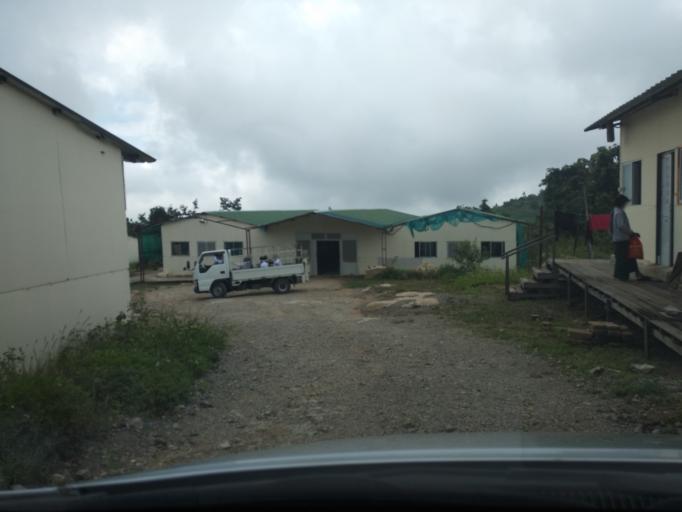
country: MM
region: Mandalay
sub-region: Pyin Oo Lwin District
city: Pyin Oo Lwin
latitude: 21.9162
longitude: 96.3858
